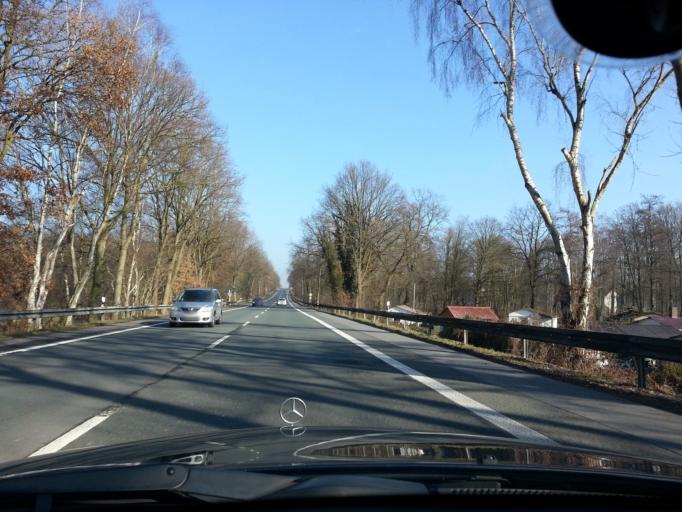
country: DE
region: North Rhine-Westphalia
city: Herten
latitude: 51.5625
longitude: 7.1216
